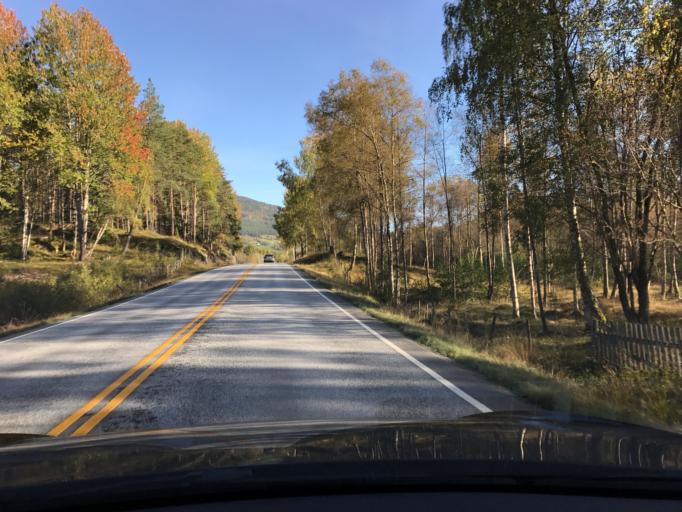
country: NO
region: Sogn og Fjordane
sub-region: Sogndal
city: Sogndalsfjora
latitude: 61.2067
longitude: 7.1928
